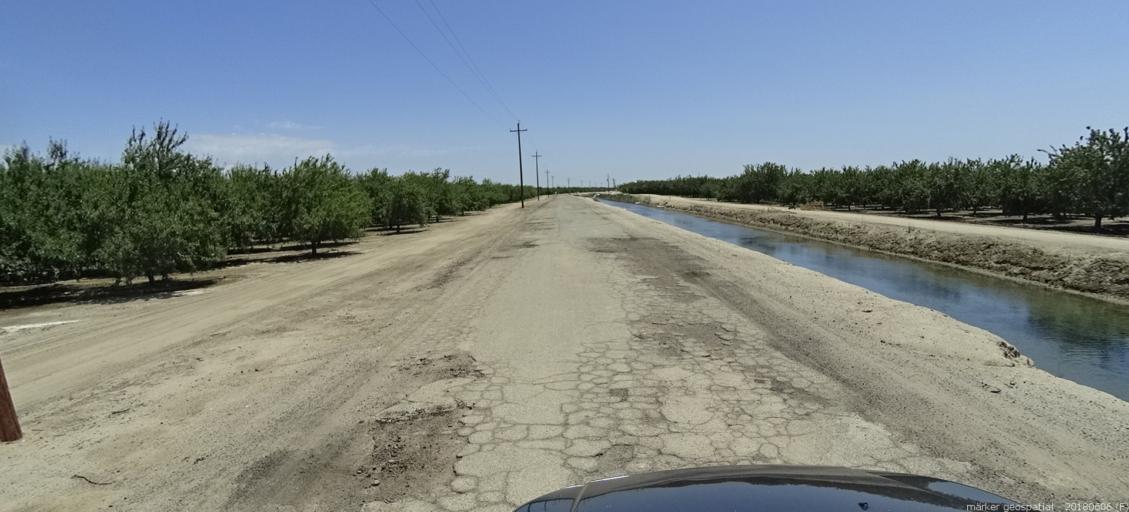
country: US
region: California
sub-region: Fresno County
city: Mendota
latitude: 36.7904
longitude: -120.3185
